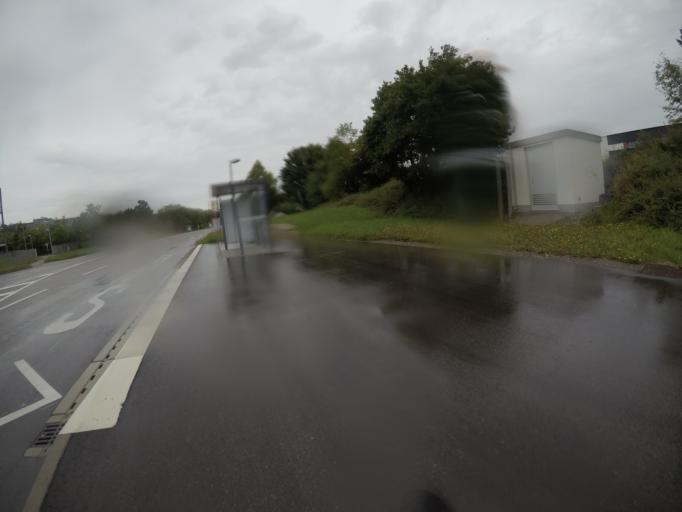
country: DE
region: Baden-Wuerttemberg
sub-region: Regierungsbezirk Stuttgart
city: Ehningen
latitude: 48.6547
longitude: 8.9449
